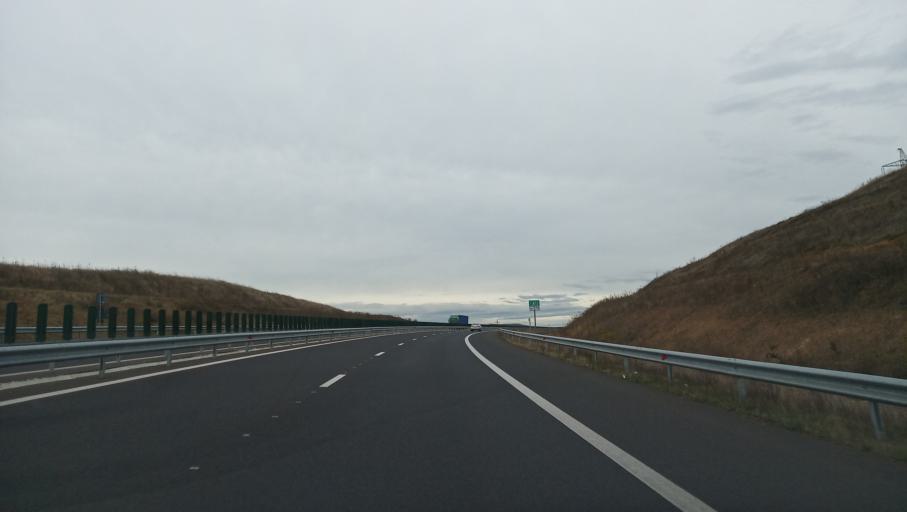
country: RO
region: Hunedoara
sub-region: Comuna Branisca
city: Branisca
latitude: 45.9132
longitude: 22.7853
